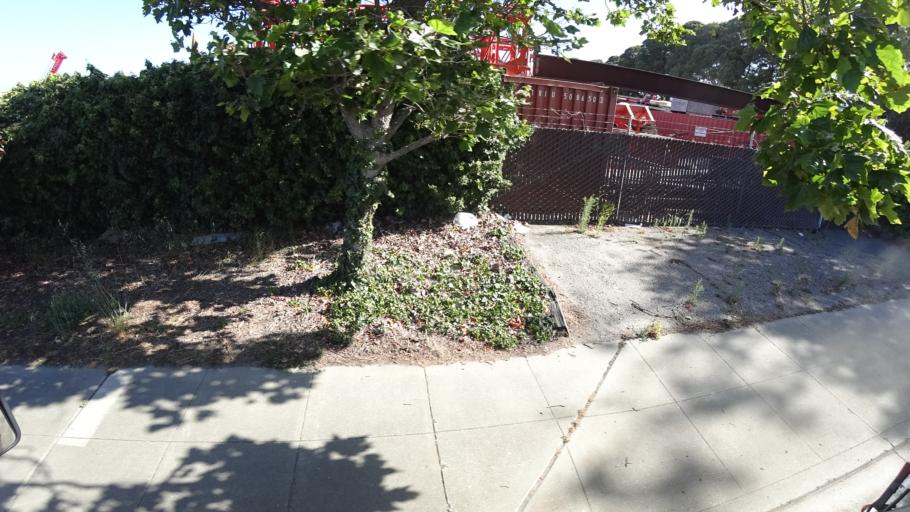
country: US
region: California
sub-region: Alameda County
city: San Lorenzo
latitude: 37.6384
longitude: -122.1273
